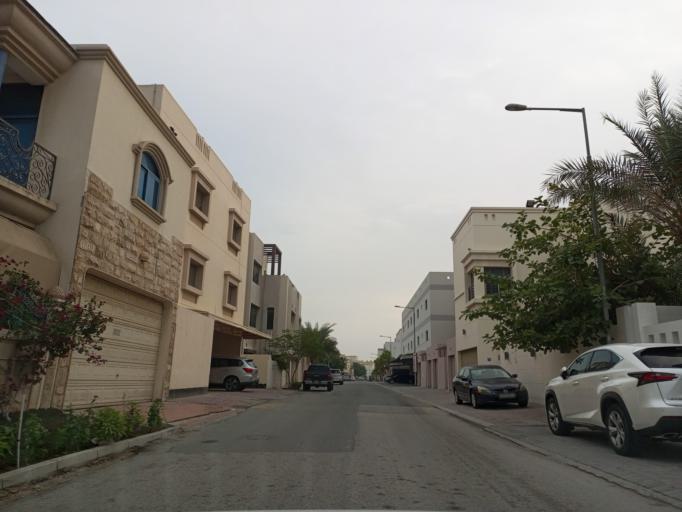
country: BH
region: Muharraq
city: Al Hadd
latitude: 26.2457
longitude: 50.6417
